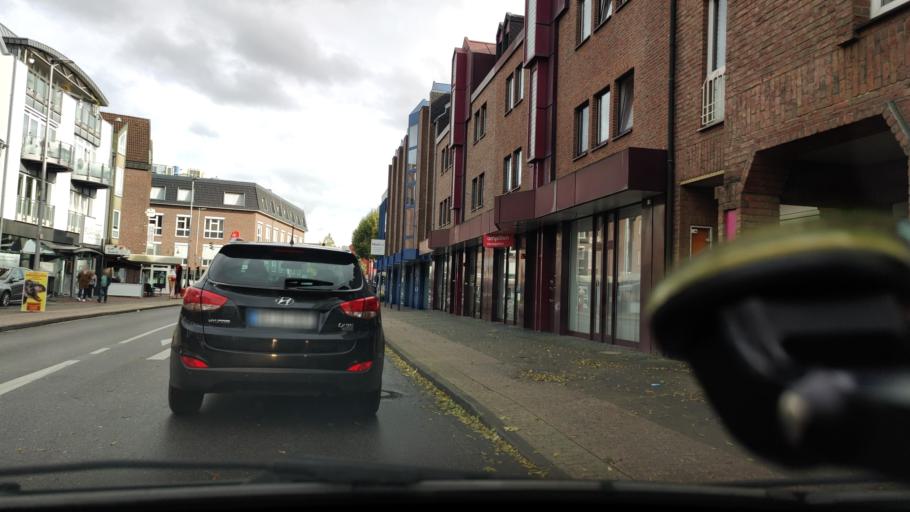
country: DE
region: North Rhine-Westphalia
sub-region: Regierungsbezirk Koln
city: Heinsberg
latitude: 51.0642
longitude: 6.0933
